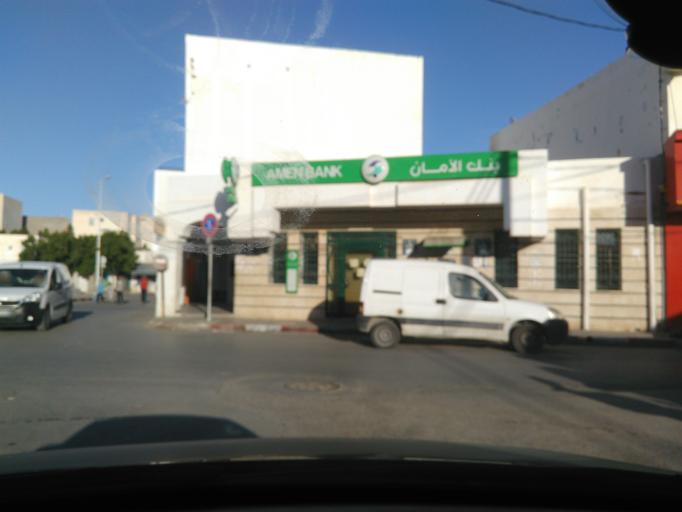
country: TN
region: Tataouine
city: Tataouine
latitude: 32.9292
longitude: 10.4485
